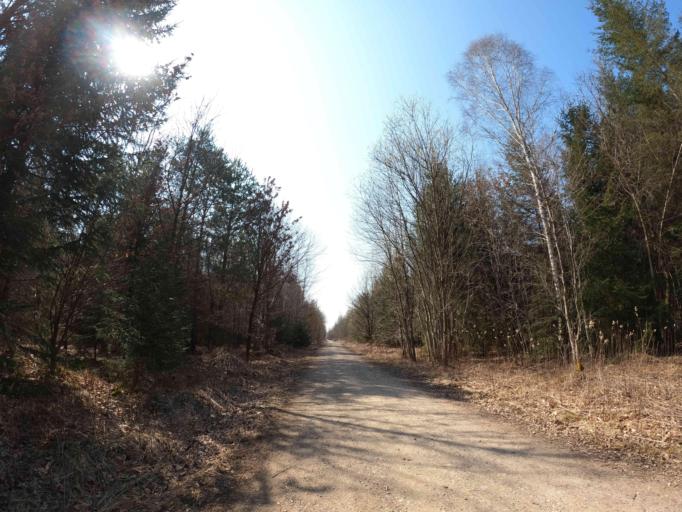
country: DE
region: Bavaria
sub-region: Upper Bavaria
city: Neuried
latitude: 48.0627
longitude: 11.4640
